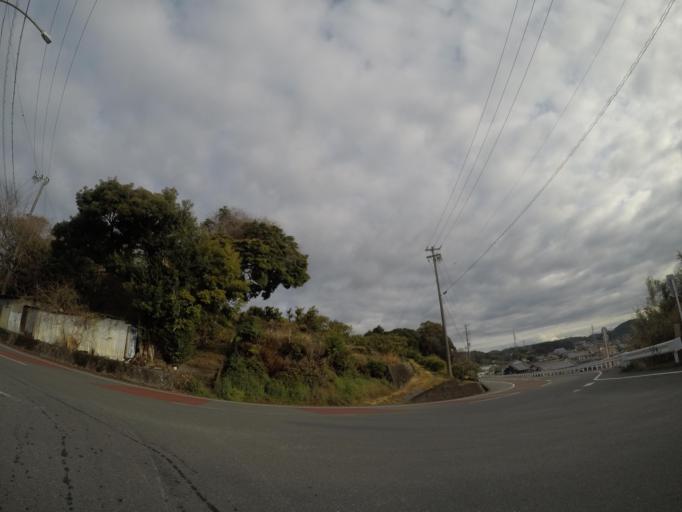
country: JP
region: Shizuoka
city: Hamakita
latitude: 34.8226
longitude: 137.7604
